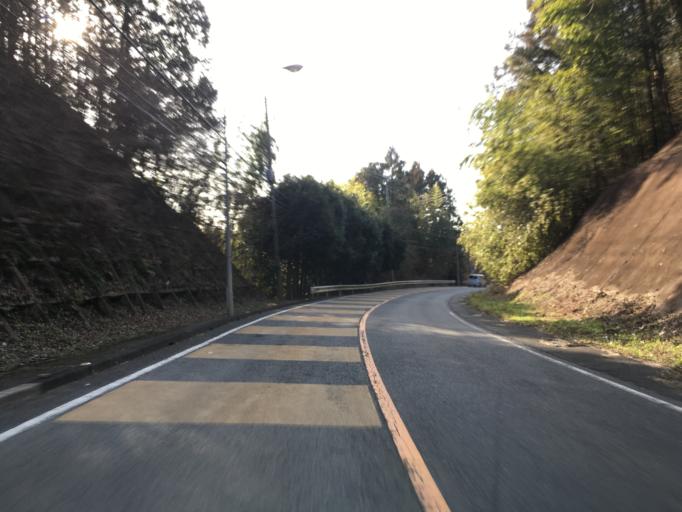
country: JP
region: Ibaraki
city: Daigo
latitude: 36.7495
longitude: 140.3979
